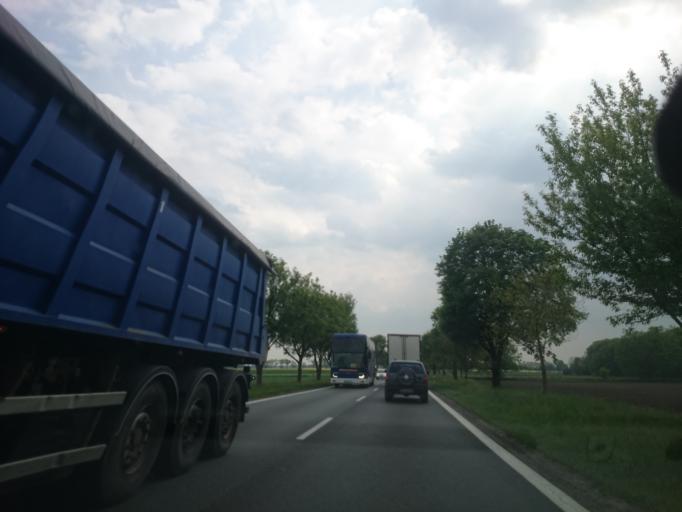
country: PL
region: Lower Silesian Voivodeship
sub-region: Powiat wroclawski
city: Kobierzyce
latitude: 50.9790
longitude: 16.9470
